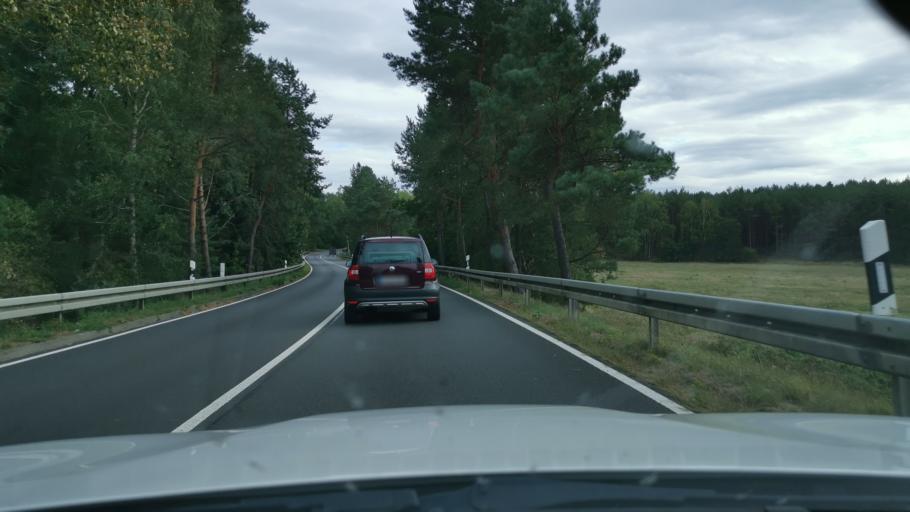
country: DE
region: Brandenburg
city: Wittstock
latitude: 53.1018
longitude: 12.4832
